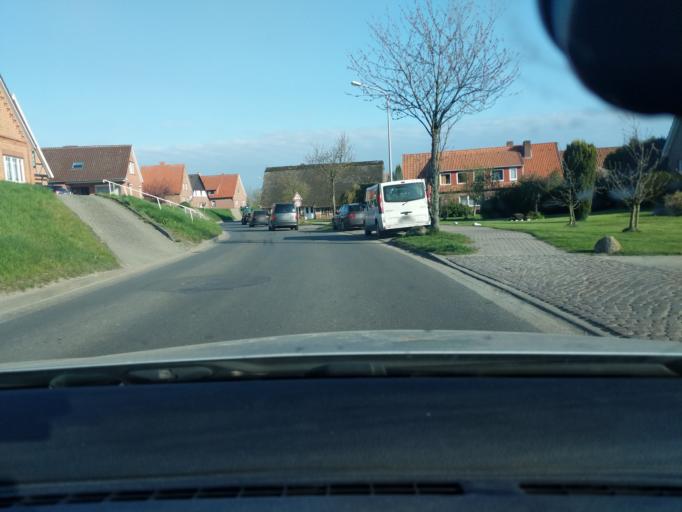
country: DE
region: Lower Saxony
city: Guderhandviertel
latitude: 53.5530
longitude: 9.6082
